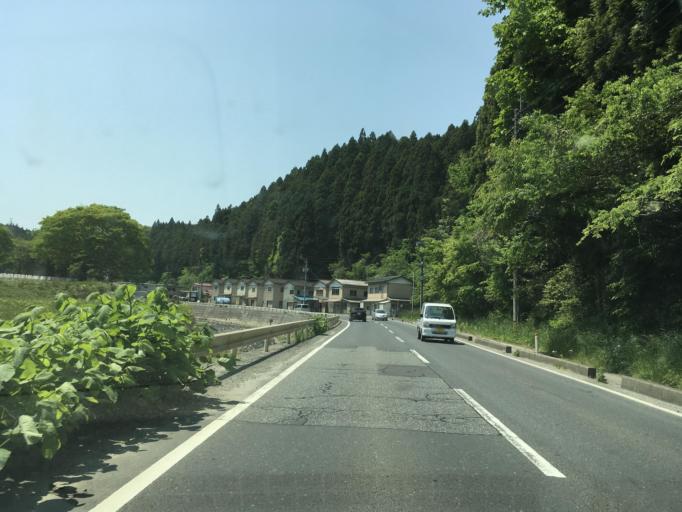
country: JP
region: Iwate
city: Ofunato
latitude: 38.8853
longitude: 141.5483
